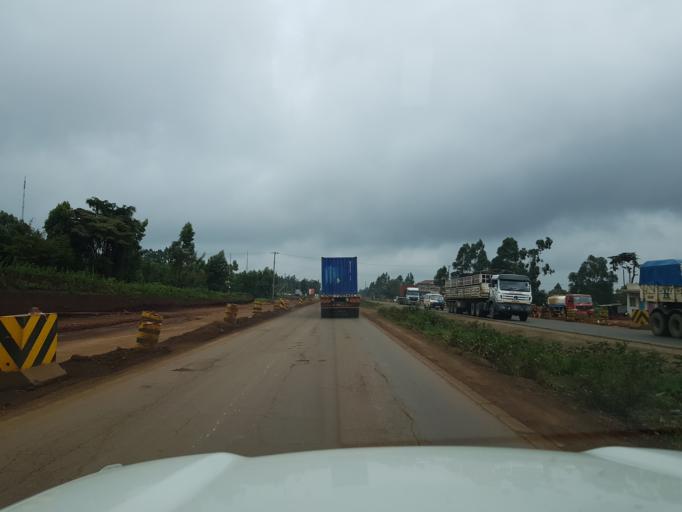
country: KE
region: Kiambu
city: Limuru
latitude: -1.1364
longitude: 36.6357
